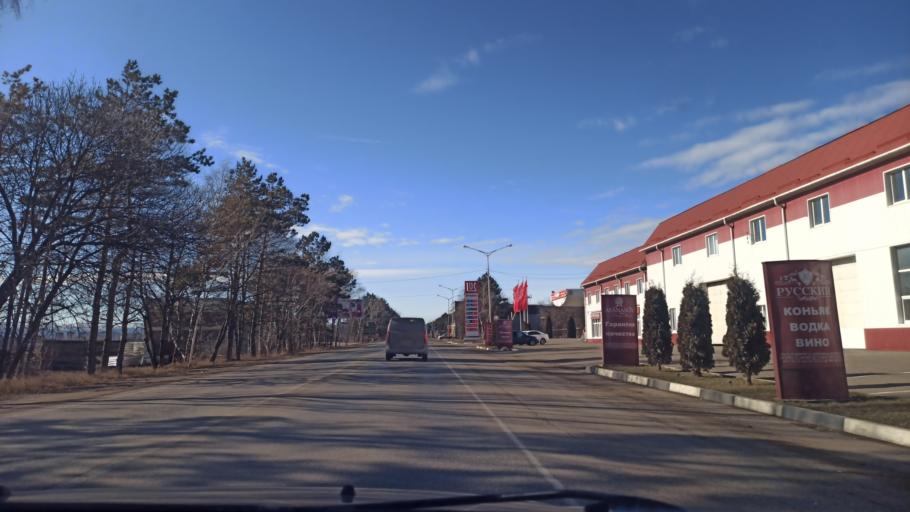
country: RU
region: Stavropol'skiy
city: Vinsady
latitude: 44.0546
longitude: 42.9271
